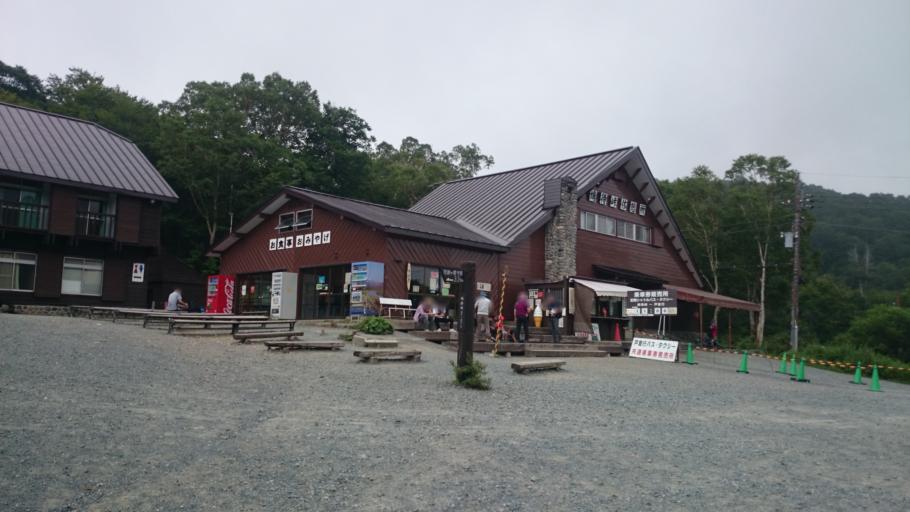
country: JP
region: Gunma
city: Numata
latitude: 36.8903
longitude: 139.2004
